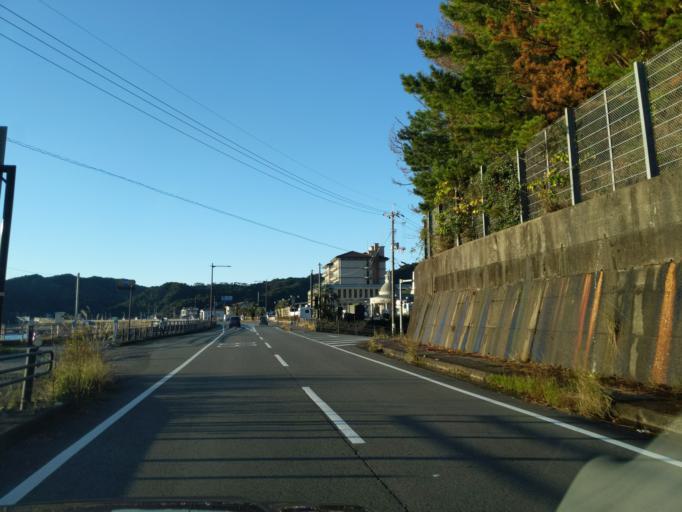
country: JP
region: Kochi
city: Muroto-misakicho
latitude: 33.5701
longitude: 134.3082
